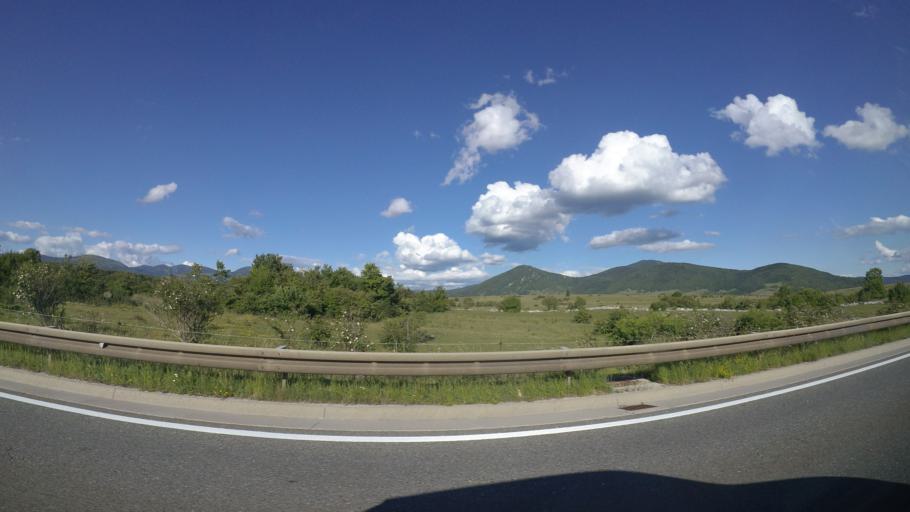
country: HR
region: Zadarska
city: Gracac
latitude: 44.5139
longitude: 15.7444
